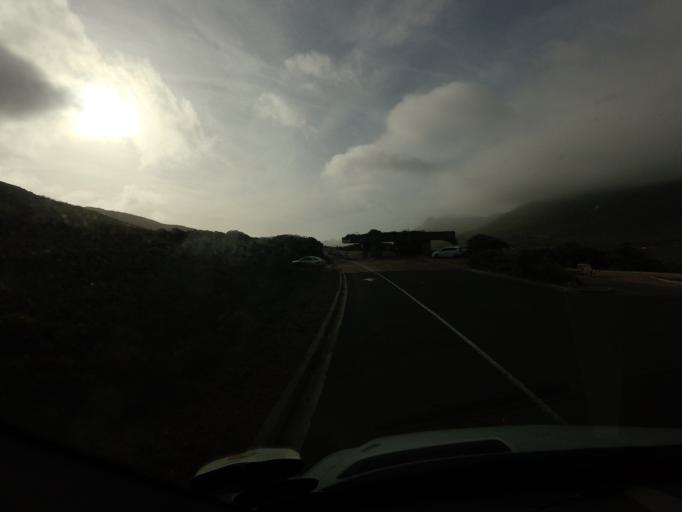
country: ZA
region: Western Cape
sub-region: City of Cape Town
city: Retreat
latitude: -34.2619
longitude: 18.4584
